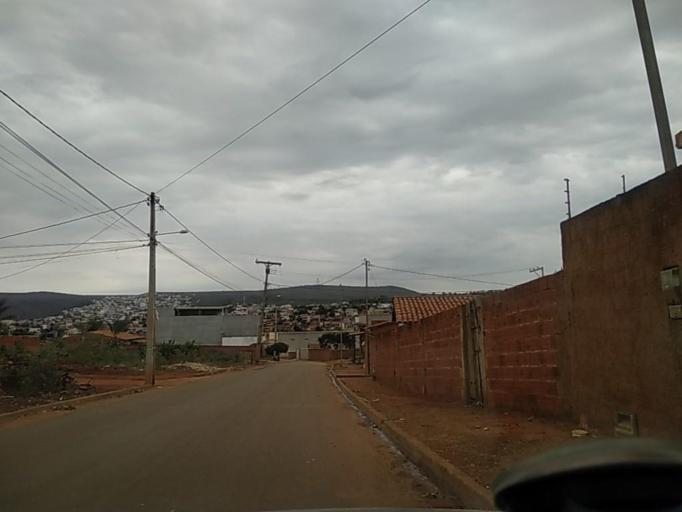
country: BR
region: Bahia
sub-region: Caetite
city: Caetite
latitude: -14.0515
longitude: -42.4755
